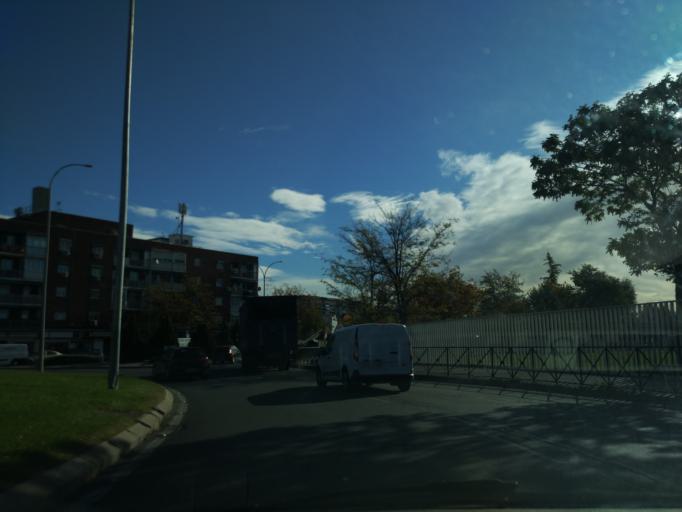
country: ES
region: Madrid
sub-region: Provincia de Madrid
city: Torrejon de Ardoz
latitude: 40.4483
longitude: -3.4695
